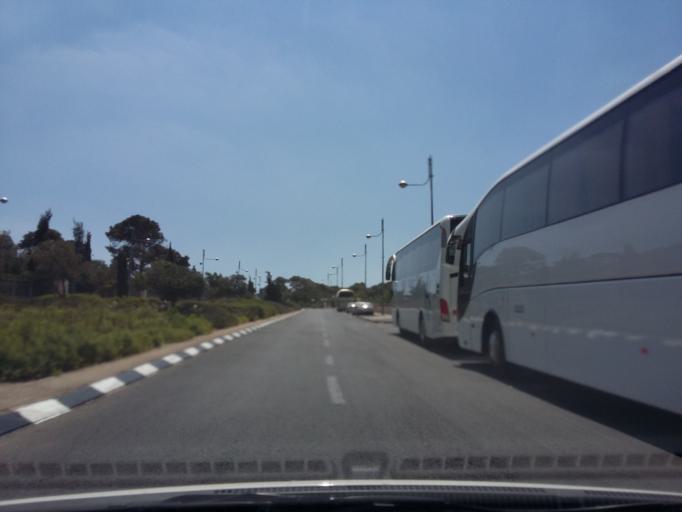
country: PS
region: West Bank
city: East Jerusalem
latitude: 31.7899
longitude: 35.2442
